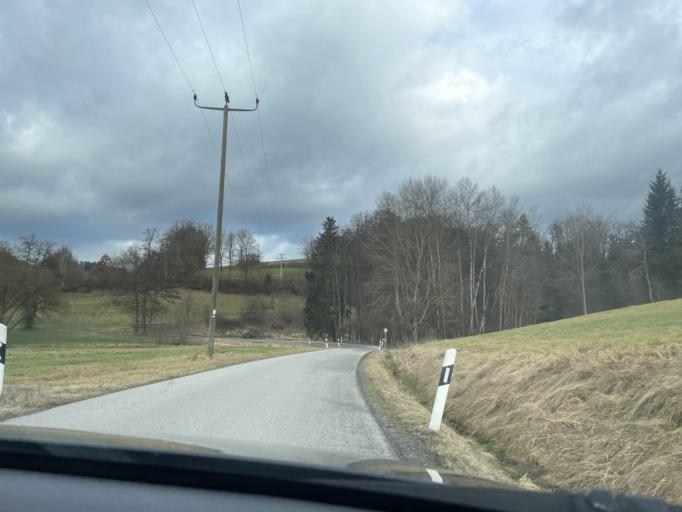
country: DE
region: Bavaria
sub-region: Lower Bavaria
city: Prackenbach
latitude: 49.1324
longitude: 12.8360
